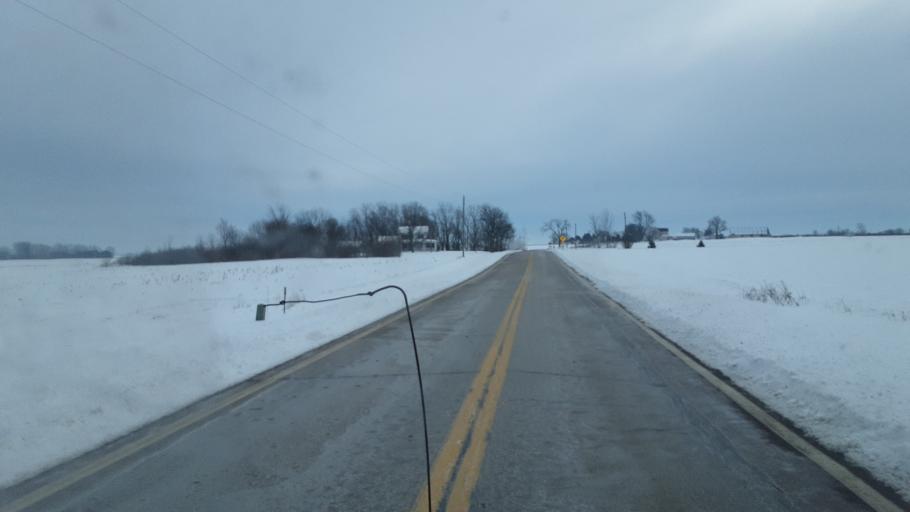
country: US
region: Ohio
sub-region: Champaign County
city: Mechanicsburg
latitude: 40.0214
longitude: -83.5172
